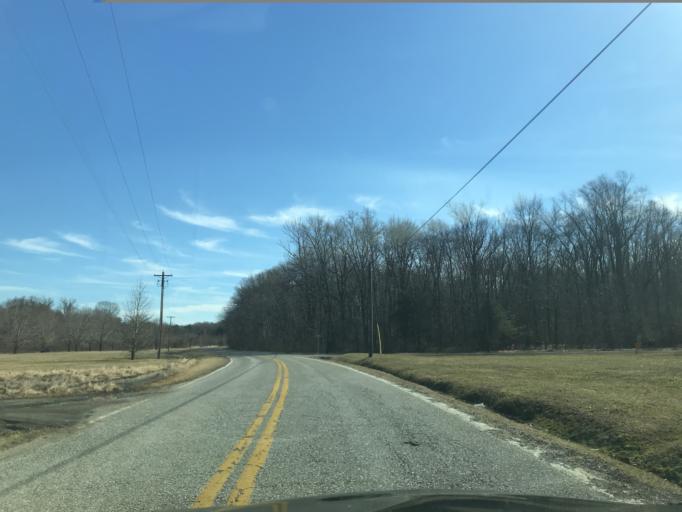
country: US
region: Virginia
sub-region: Fairfax County
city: Mount Vernon
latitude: 38.6834
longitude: -77.0989
